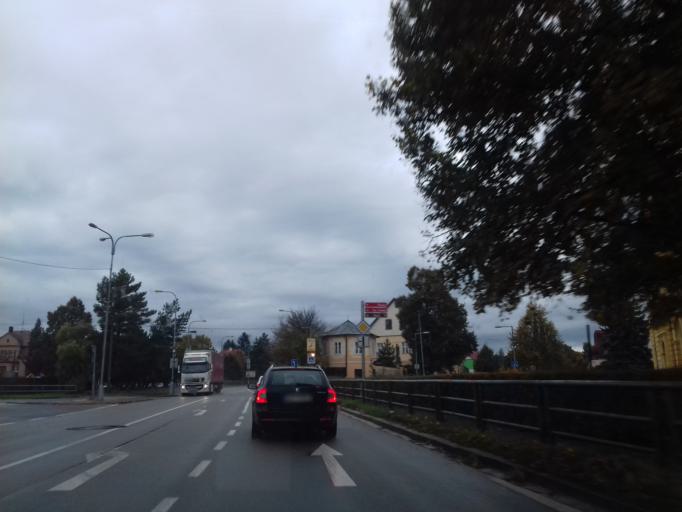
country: CZ
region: Pardubicky
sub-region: Okres Pardubice
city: Vysoke Myto
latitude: 49.9474
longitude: 16.1601
